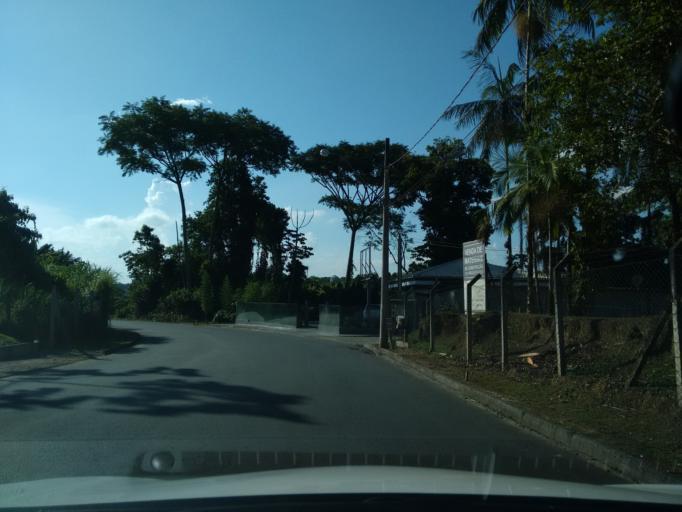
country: BR
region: Santa Catarina
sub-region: Blumenau
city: Blumenau
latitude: -26.8972
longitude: -49.0657
